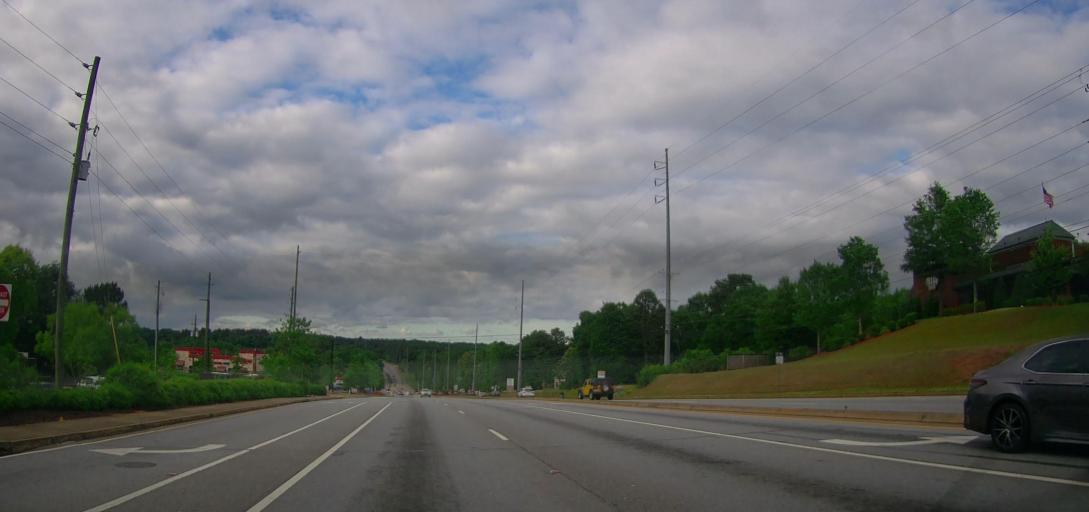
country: US
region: Georgia
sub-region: Oconee County
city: Watkinsville
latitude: 33.9187
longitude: -83.4426
